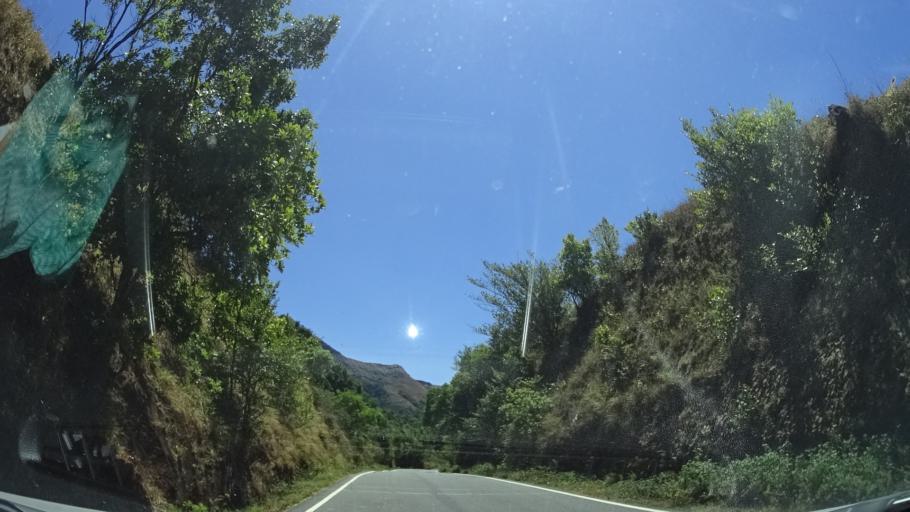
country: IN
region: Karnataka
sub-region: Udupi
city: Karkal
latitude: 13.2536
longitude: 75.1647
